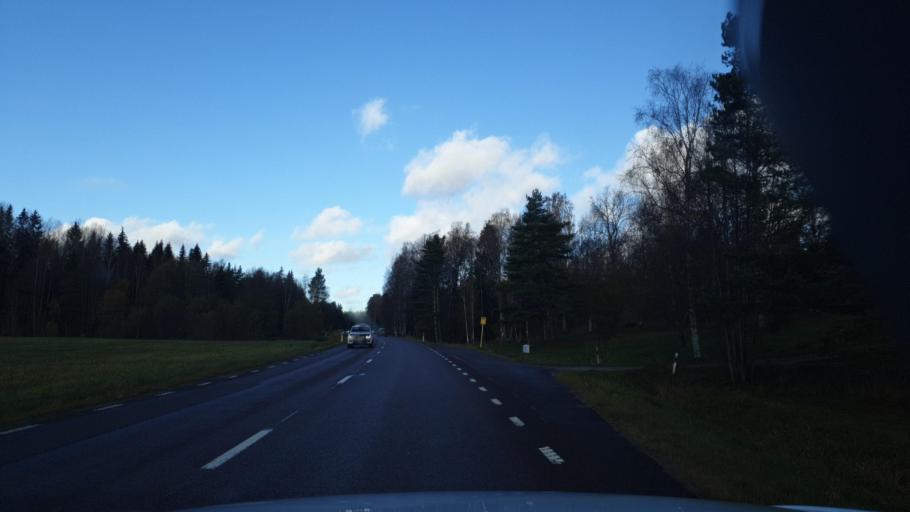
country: SE
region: Vaermland
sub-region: Arvika Kommun
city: Arvika
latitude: 59.6149
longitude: 12.6192
